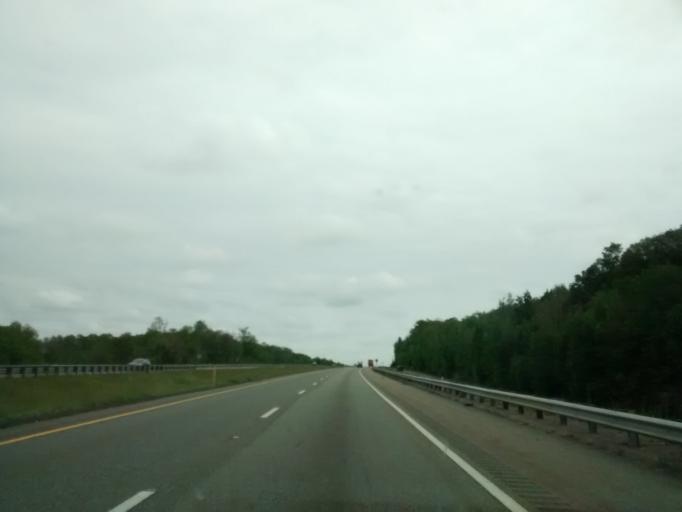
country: US
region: Massachusetts
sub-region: Worcester County
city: Uxbridge
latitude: 42.0456
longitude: -71.6277
